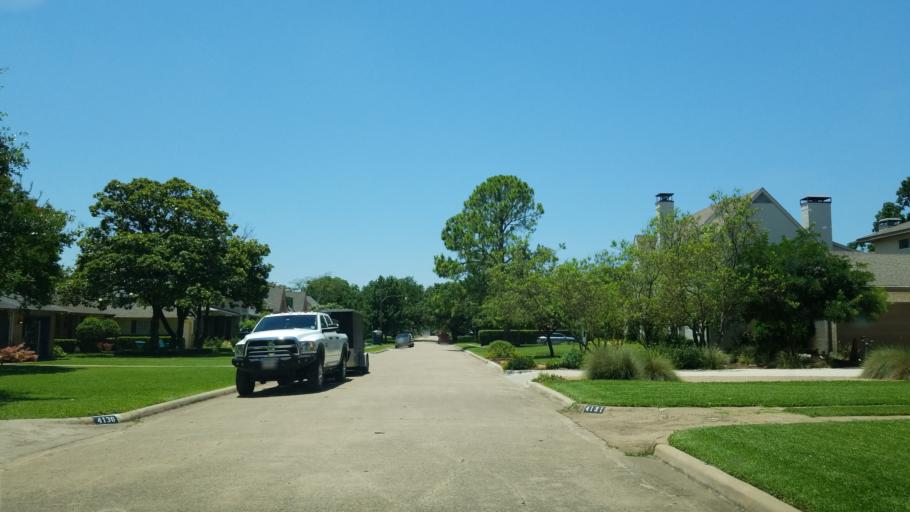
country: US
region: Texas
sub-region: Dallas County
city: University Park
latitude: 32.8718
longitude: -96.8406
